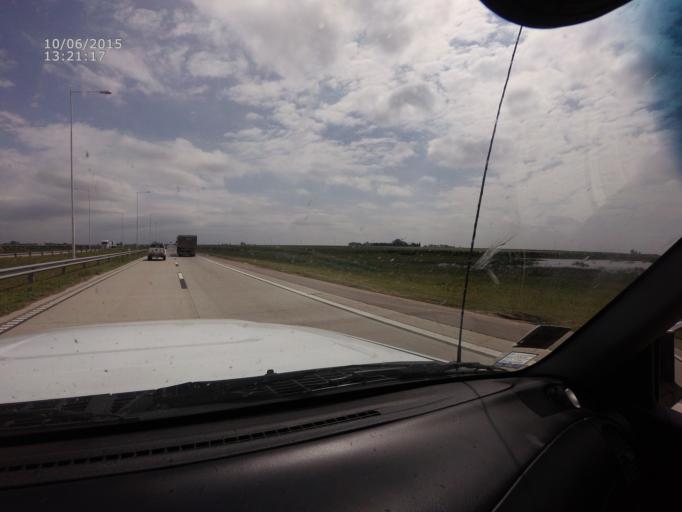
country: AR
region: Cordoba
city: Marcos Juarez
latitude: -32.6688
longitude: -62.0711
